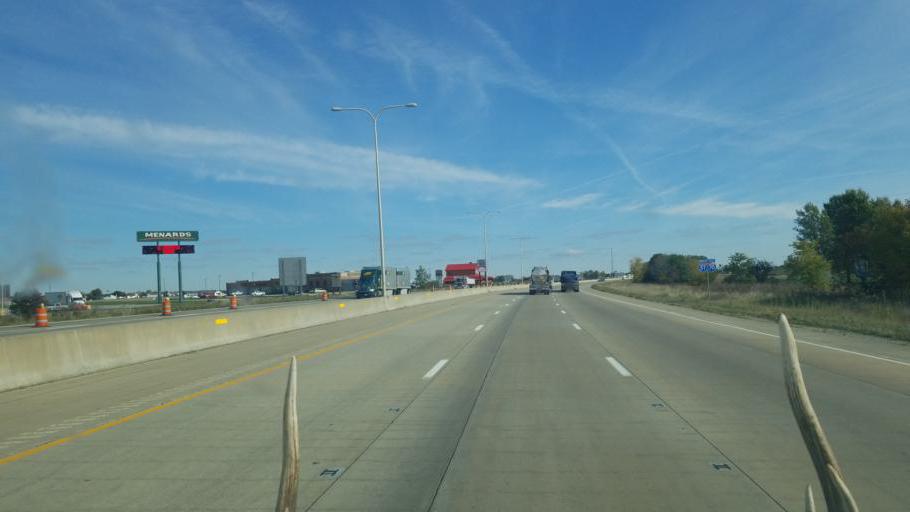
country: US
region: Illinois
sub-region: Effingham County
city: Effingham
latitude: 39.1392
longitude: -88.5574
